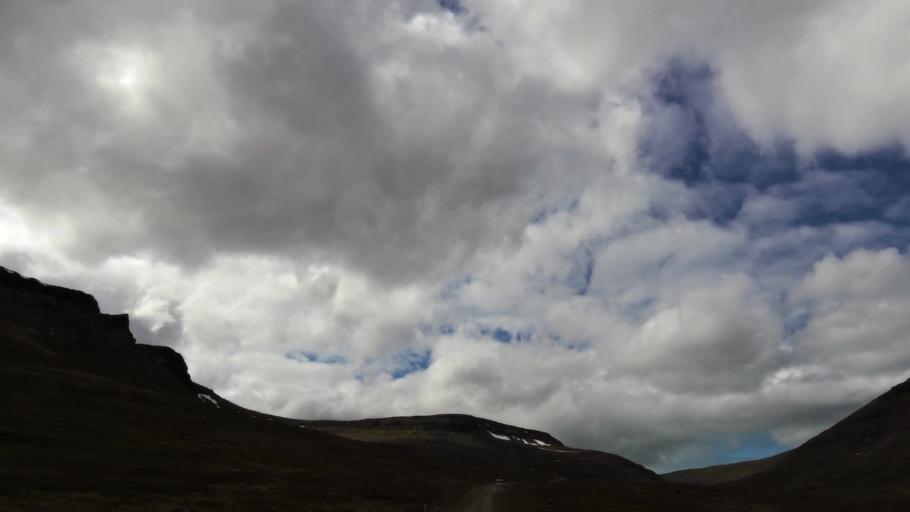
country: IS
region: Westfjords
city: Isafjoerdur
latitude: 66.1617
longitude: -23.3071
